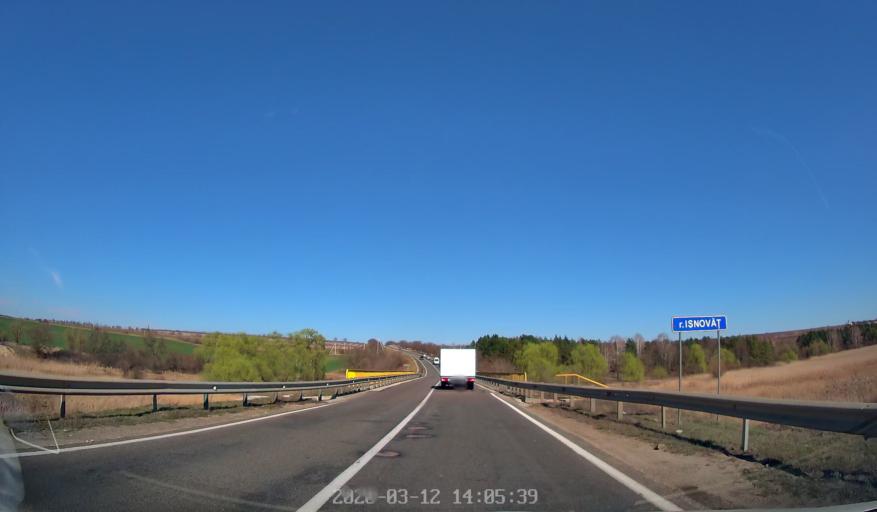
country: MD
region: Chisinau
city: Vatra
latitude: 46.9882
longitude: 28.6872
